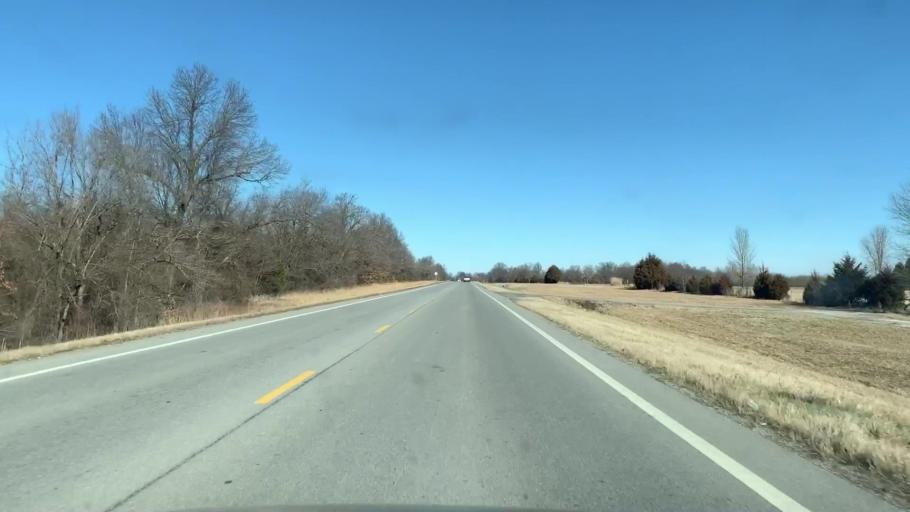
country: US
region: Kansas
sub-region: Cherokee County
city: Baxter Springs
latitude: 37.0415
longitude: -94.7360
